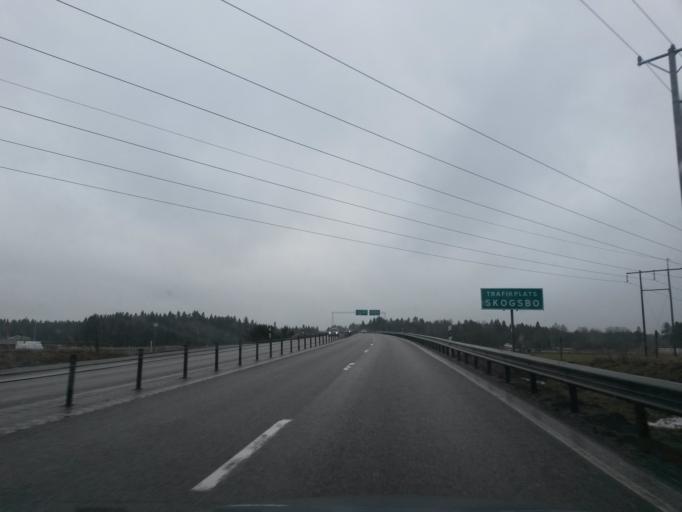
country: SE
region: Vaestra Goetaland
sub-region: Vanersborgs Kommun
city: Vanersborg
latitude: 58.3430
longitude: 12.3056
